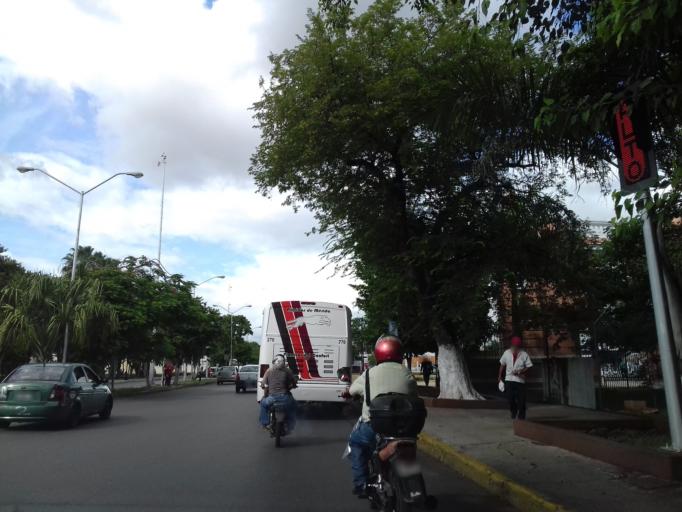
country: MX
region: Yucatan
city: Merida
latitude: 20.9709
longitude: -89.6407
